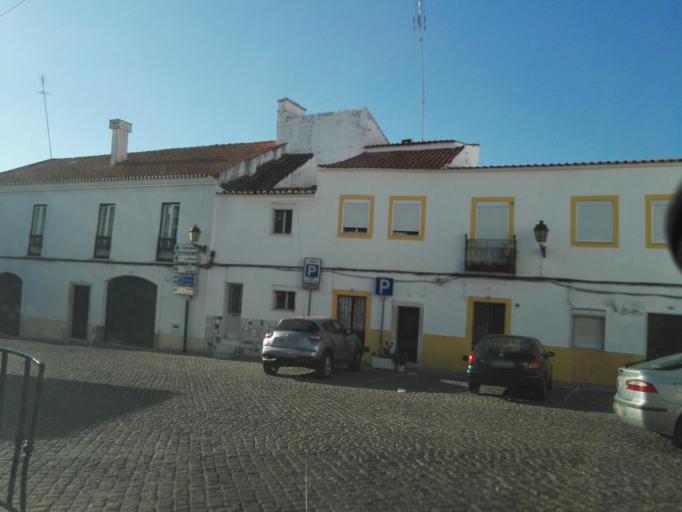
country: PT
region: Portalegre
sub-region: Elvas
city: Elvas
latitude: 38.8819
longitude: -7.1644
